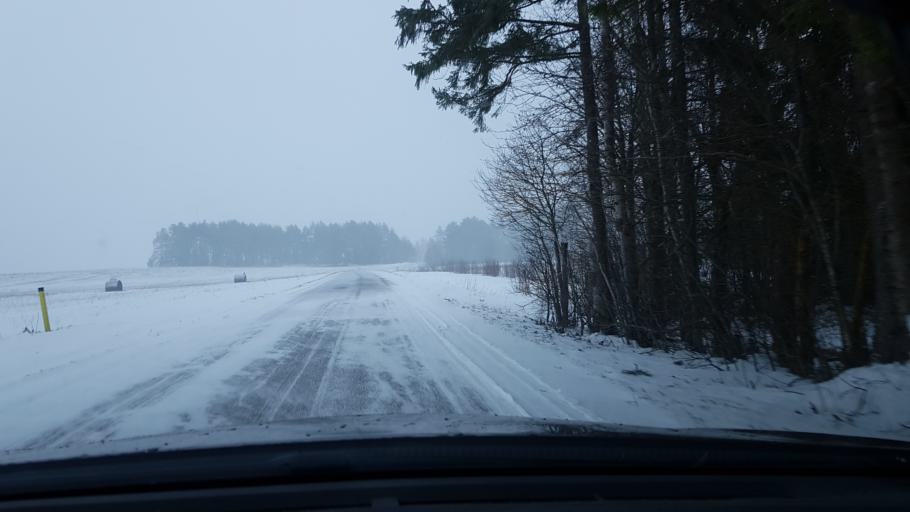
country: EE
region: Harju
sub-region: Anija vald
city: Kehra
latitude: 59.2000
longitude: 25.4038
